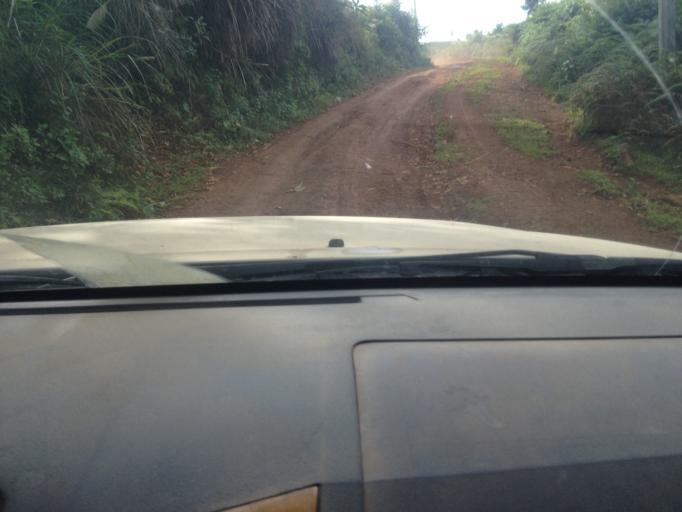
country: TH
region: Nan
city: Chaloem Phra Kiat
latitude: 19.9618
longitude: 101.0192
